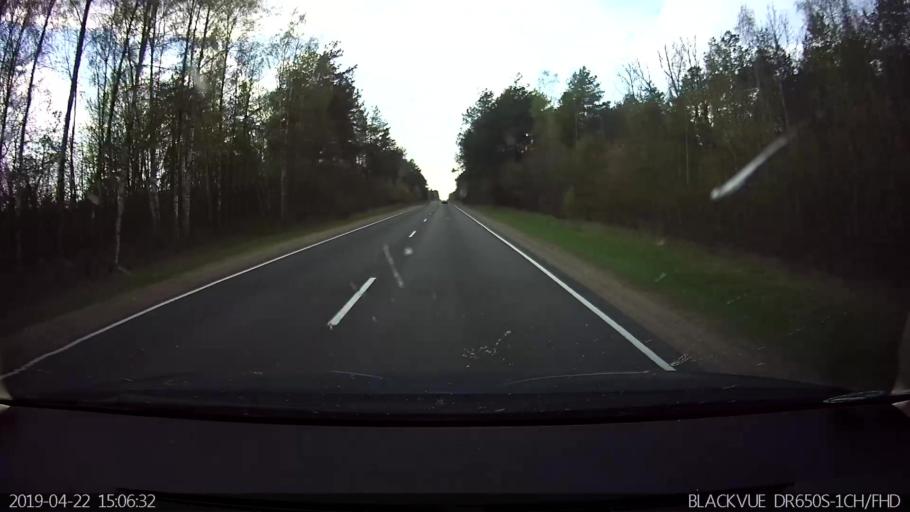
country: BY
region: Brest
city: Kamyanyets
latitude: 52.3313
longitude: 23.8341
